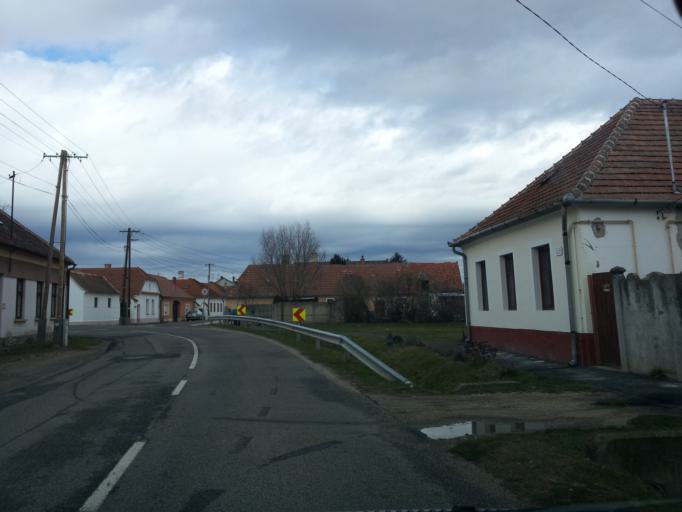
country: HU
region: Vas
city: Koszeg
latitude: 47.3417
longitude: 16.5744
